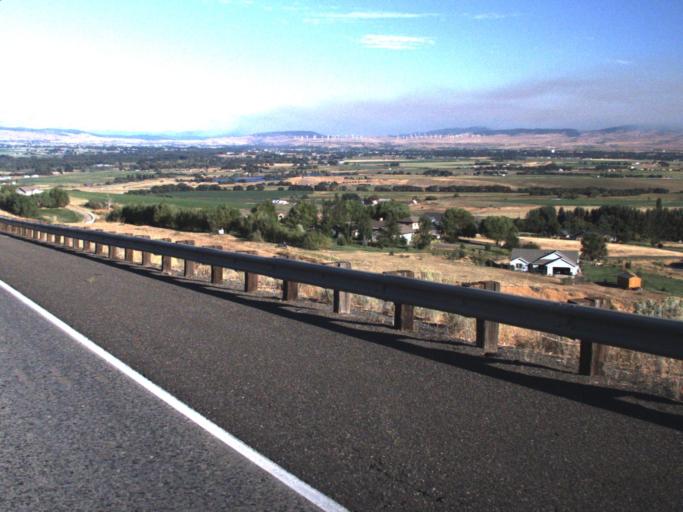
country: US
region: Washington
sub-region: Kittitas County
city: Kittitas
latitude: 46.9117
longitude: -120.4710
